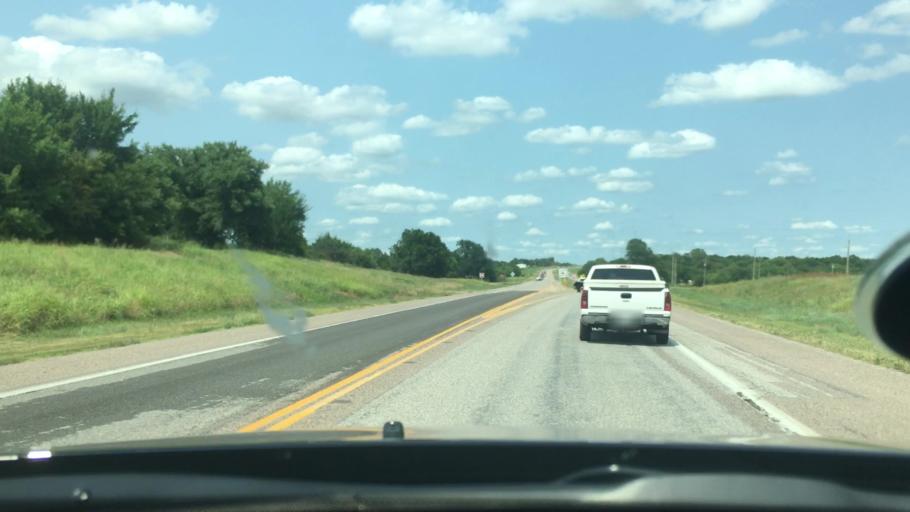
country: US
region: Oklahoma
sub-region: Pontotoc County
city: Ada
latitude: 34.6627
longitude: -96.7899
